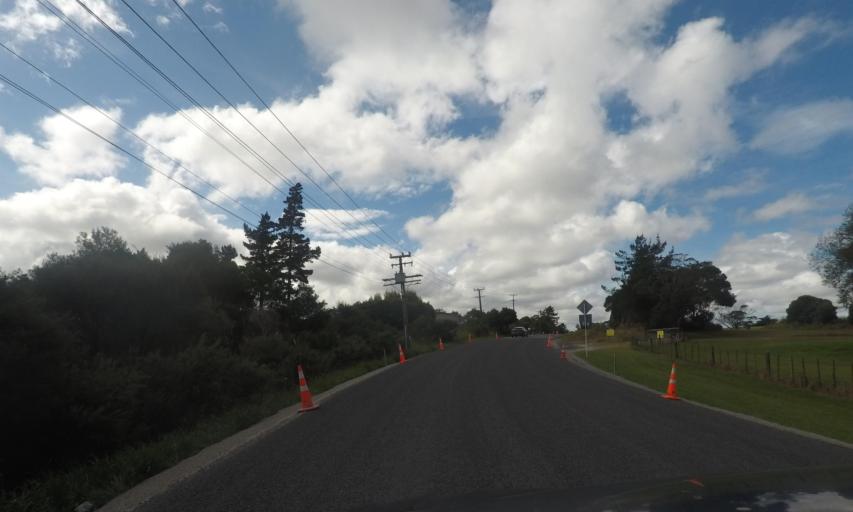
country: NZ
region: Auckland
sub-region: Auckland
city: Rosebank
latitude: -36.7902
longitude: 174.6372
